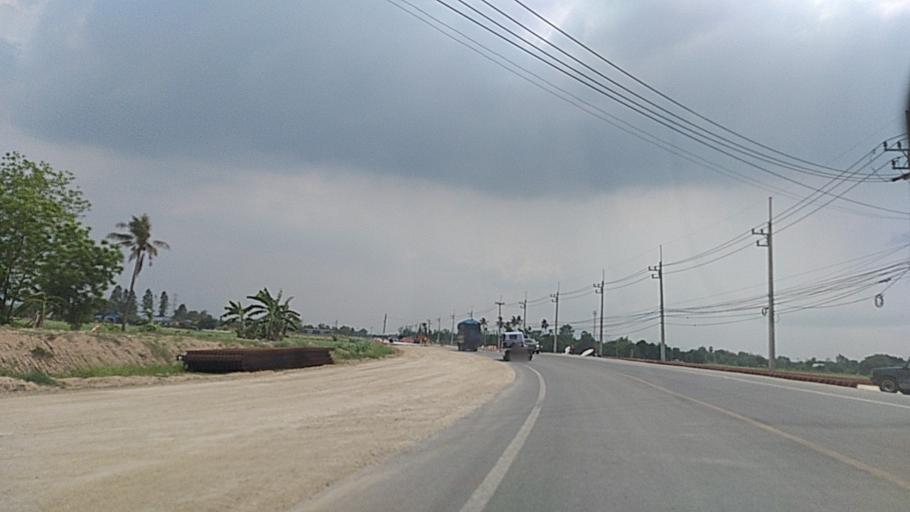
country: TH
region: Chon Buri
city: Ban Bueng
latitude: 13.3352
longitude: 101.1883
